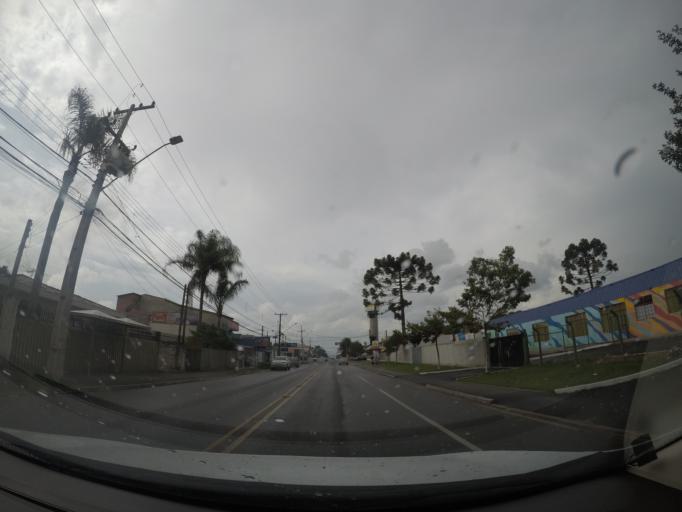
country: BR
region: Parana
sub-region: Sao Jose Dos Pinhais
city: Sao Jose dos Pinhais
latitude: -25.5150
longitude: -49.2446
